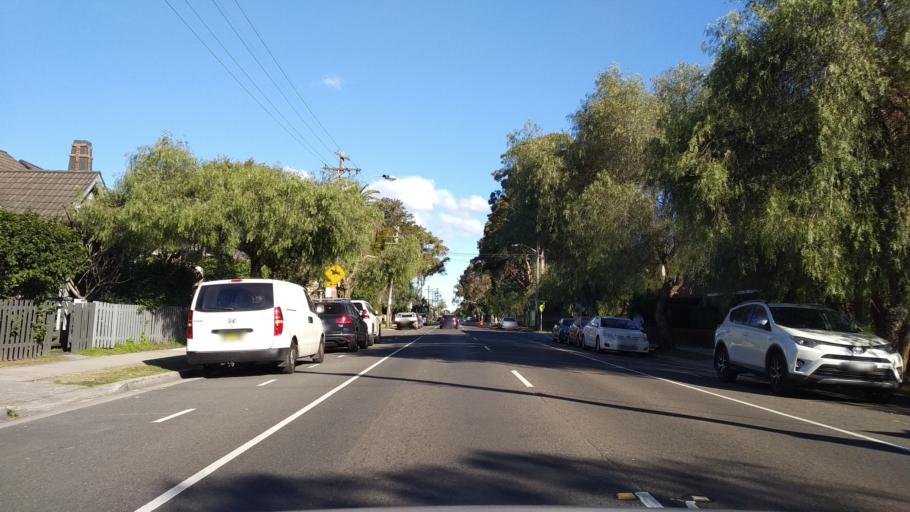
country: AU
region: New South Wales
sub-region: Randwick
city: Kensington
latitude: -33.9086
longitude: 151.2256
